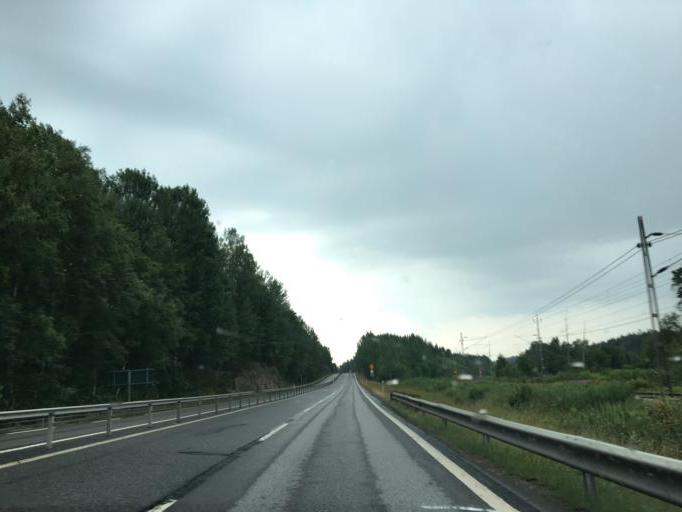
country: SE
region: OEstergoetland
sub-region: Norrkopings Kommun
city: Jursla
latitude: 58.7775
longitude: 16.1624
